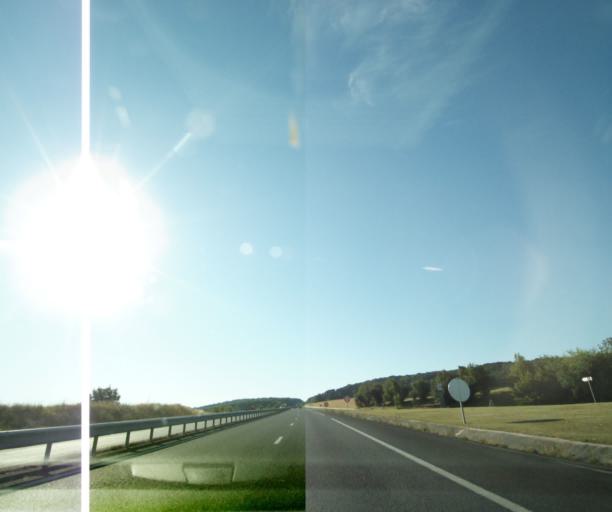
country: FR
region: Bourgogne
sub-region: Departement de l'Yonne
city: Soucy
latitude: 48.2463
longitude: 3.3501
